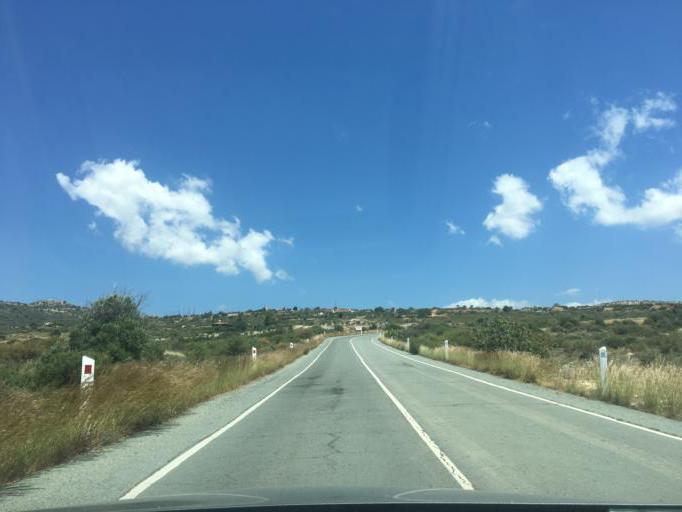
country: CY
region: Limassol
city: Mouttagiaka
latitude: 34.7395
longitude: 33.0626
